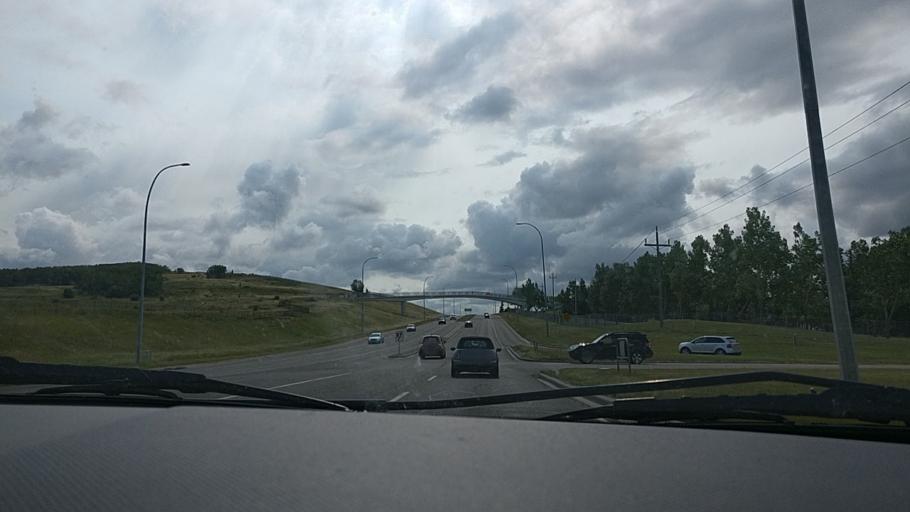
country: CA
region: Alberta
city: Calgary
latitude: 51.1033
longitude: -114.1277
